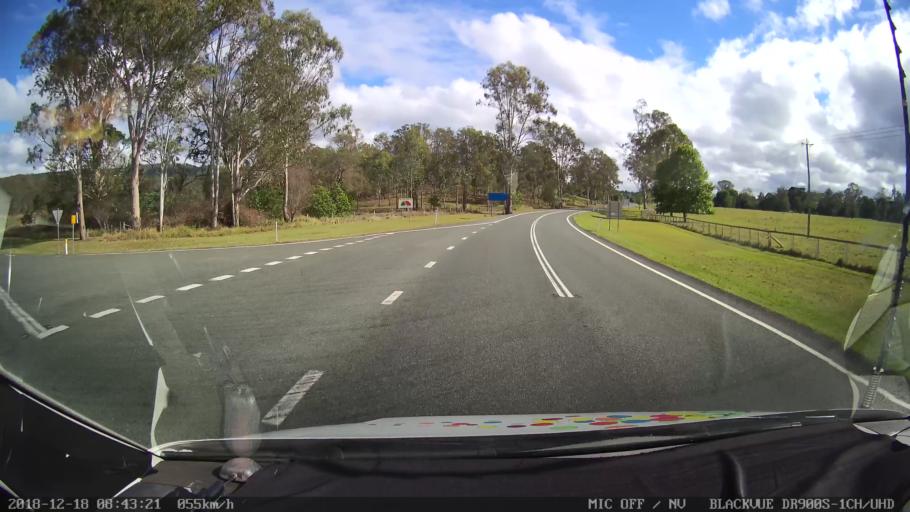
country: AU
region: Queensland
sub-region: Logan
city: Cedar Vale
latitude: -28.2190
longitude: 152.8583
